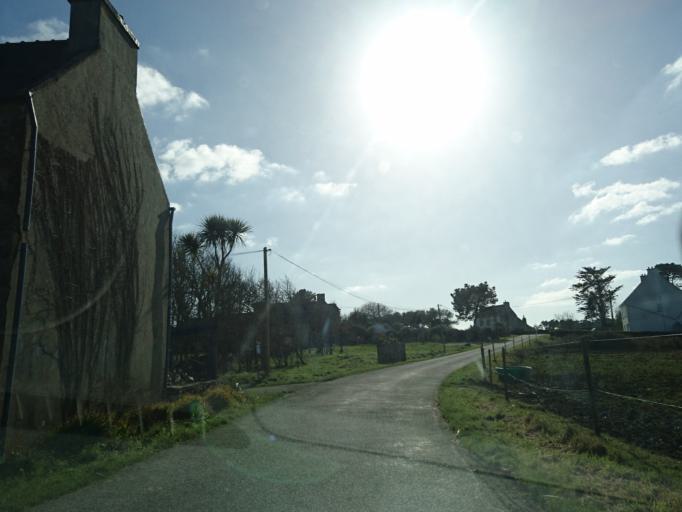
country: FR
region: Brittany
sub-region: Departement du Finistere
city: Roscanvel
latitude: 48.3255
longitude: -4.5701
